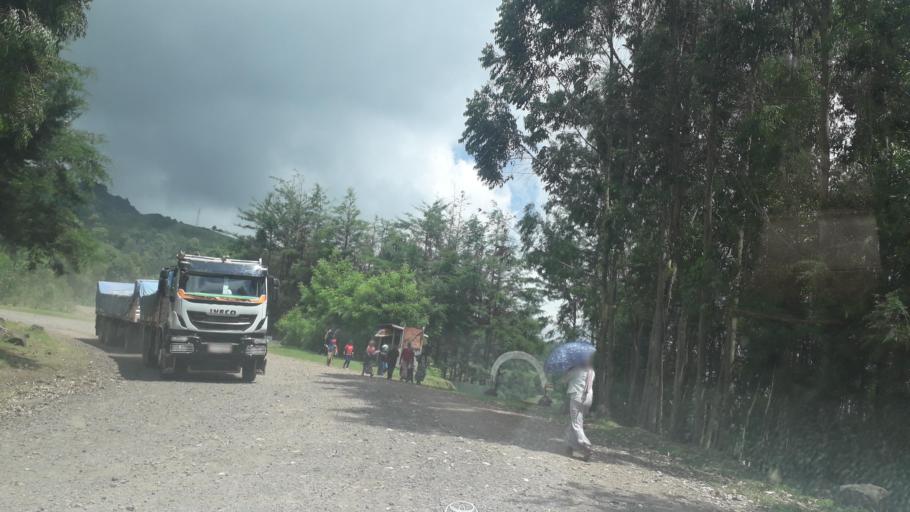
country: ET
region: Oromiya
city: Jima
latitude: 7.4260
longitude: 36.8722
